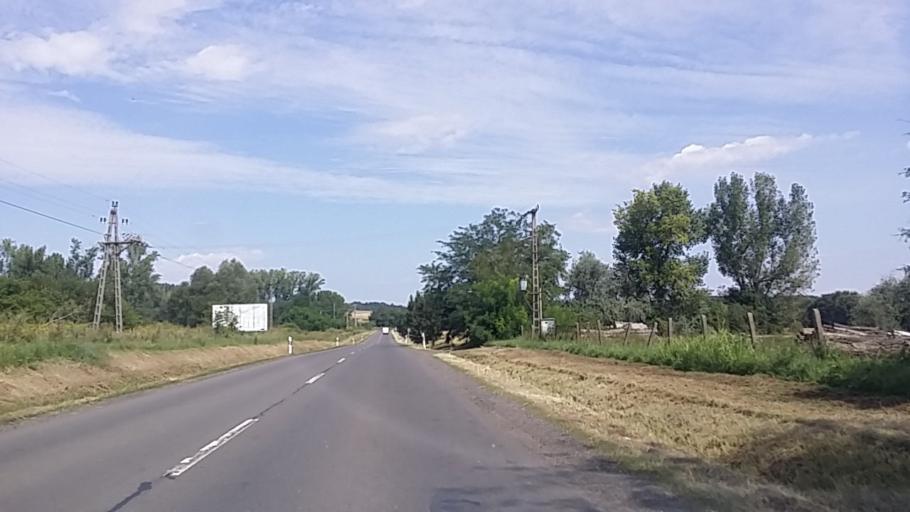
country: HU
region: Baranya
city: Sasd
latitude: 46.2672
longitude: 18.1043
